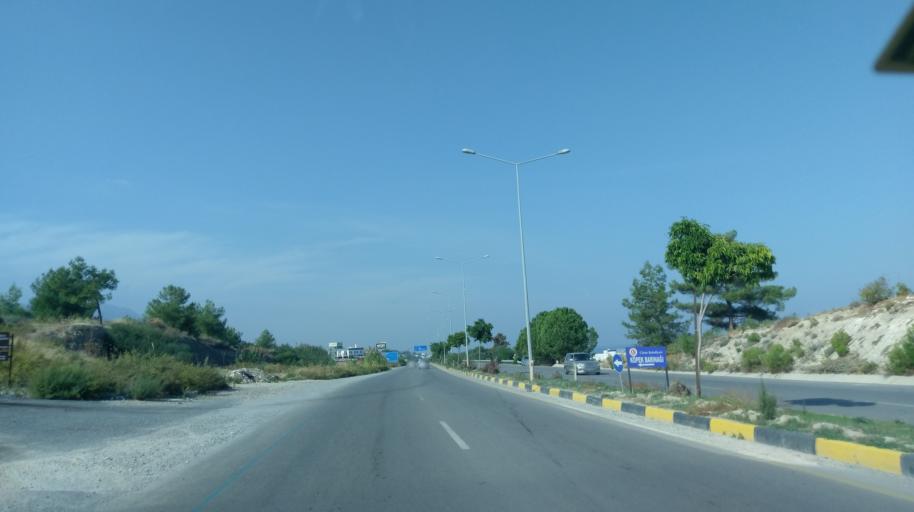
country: CY
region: Keryneia
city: Kyrenia
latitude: 35.3293
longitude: 33.2814
